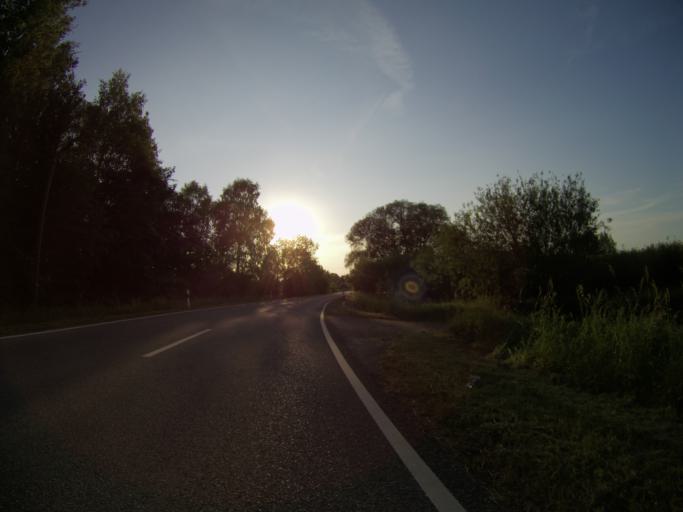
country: DE
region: Bavaria
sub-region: Upper Bavaria
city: Marzling
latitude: 48.3720
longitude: 11.7864
